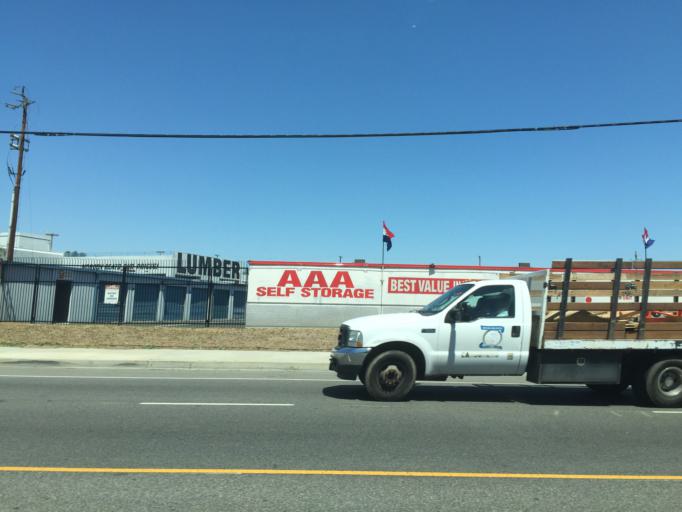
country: US
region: California
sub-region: Los Angeles County
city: Chatsworth
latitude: 34.2368
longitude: -118.6058
